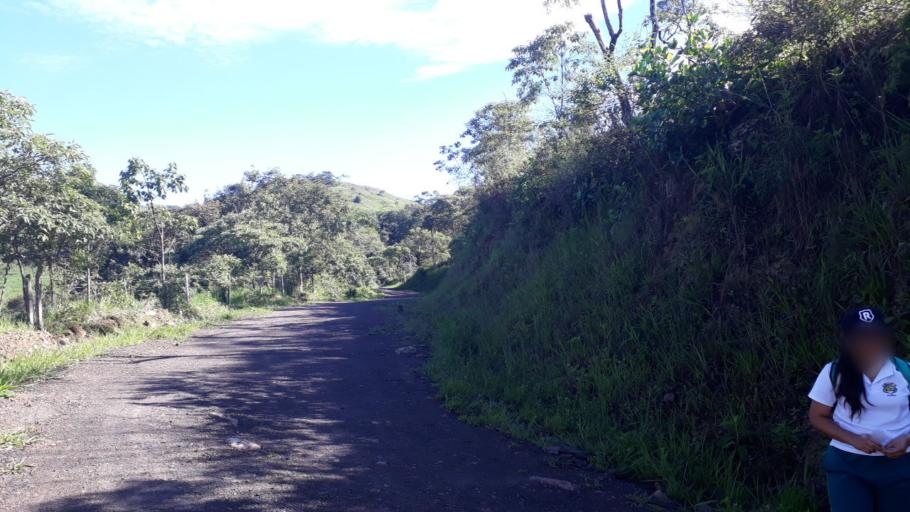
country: CO
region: Casanare
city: Nunchia
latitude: 5.6525
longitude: -72.4229
